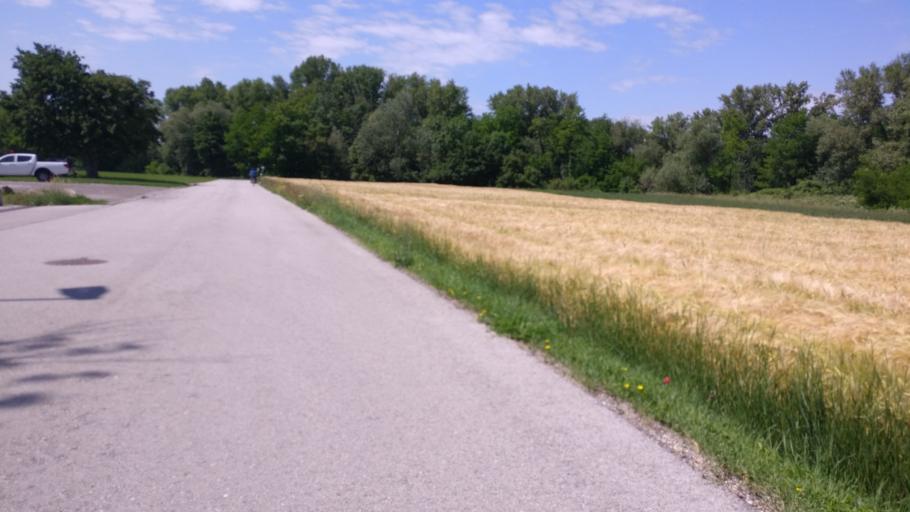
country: AT
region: Lower Austria
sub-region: Politischer Bezirk Baden
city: Gunselsdorf
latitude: 47.9462
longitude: 16.2650
